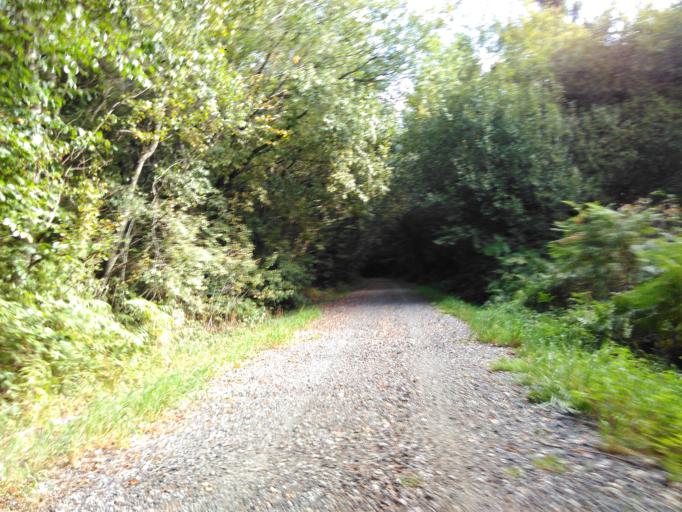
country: BE
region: Wallonia
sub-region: Province du Luxembourg
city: Vaux-sur-Sure
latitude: 49.9409
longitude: 5.5848
